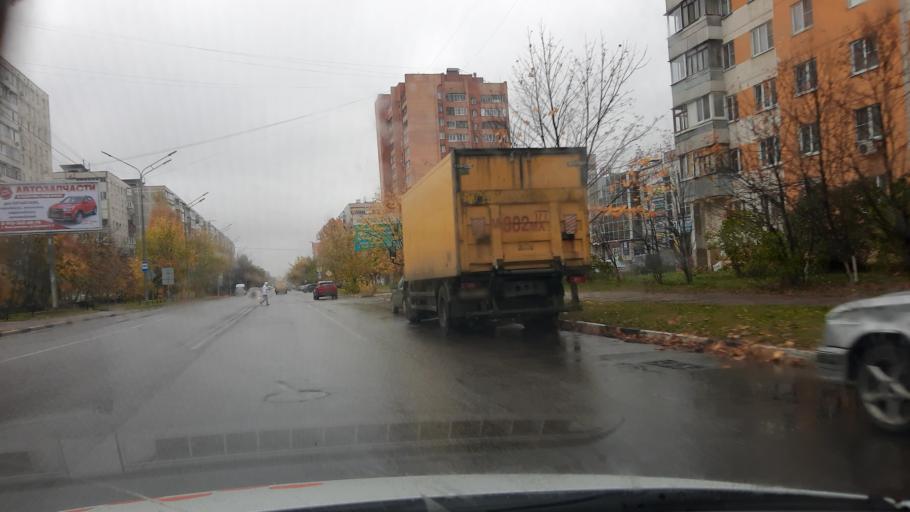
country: RU
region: Moskovskaya
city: Elektrostal'
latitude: 55.8058
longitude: 38.4355
